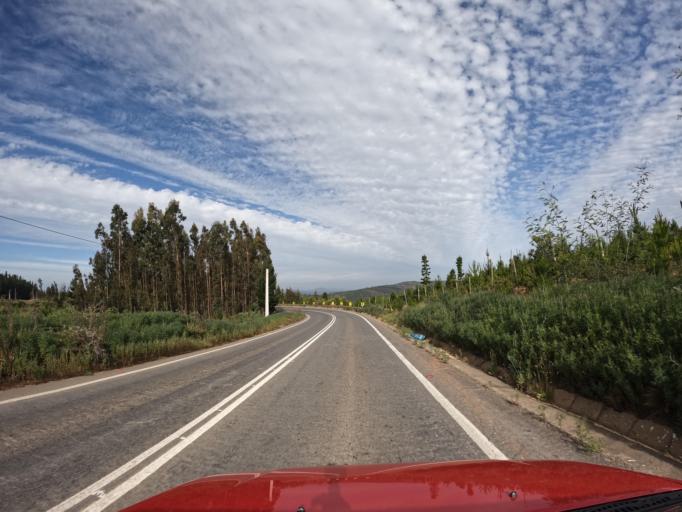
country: CL
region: O'Higgins
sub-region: Provincia de Colchagua
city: Santa Cruz
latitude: -34.3037
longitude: -71.8308
